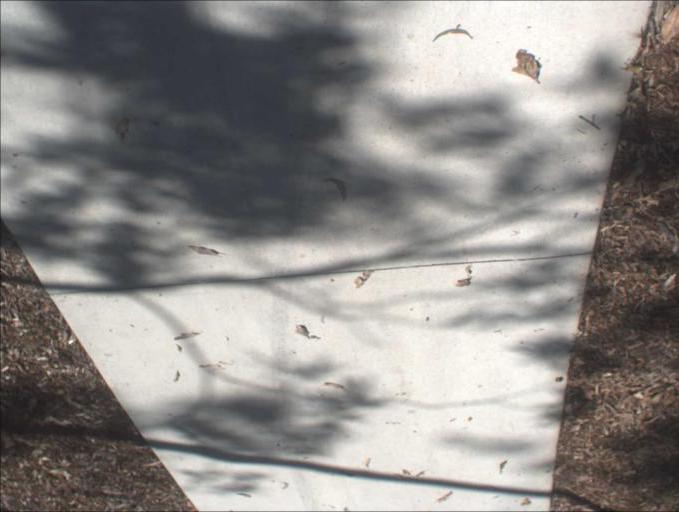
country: AU
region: Queensland
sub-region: Logan
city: Waterford West
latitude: -27.7145
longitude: 153.1533
